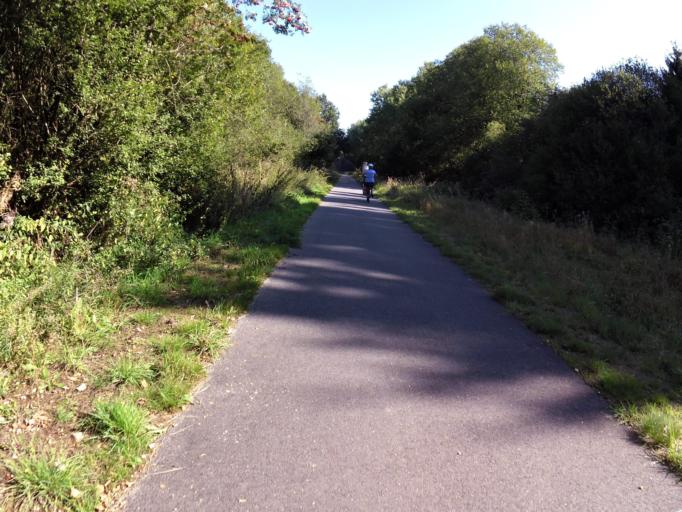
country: BE
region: Wallonia
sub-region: Province de Liege
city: Butgenbach
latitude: 50.4257
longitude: 6.1710
